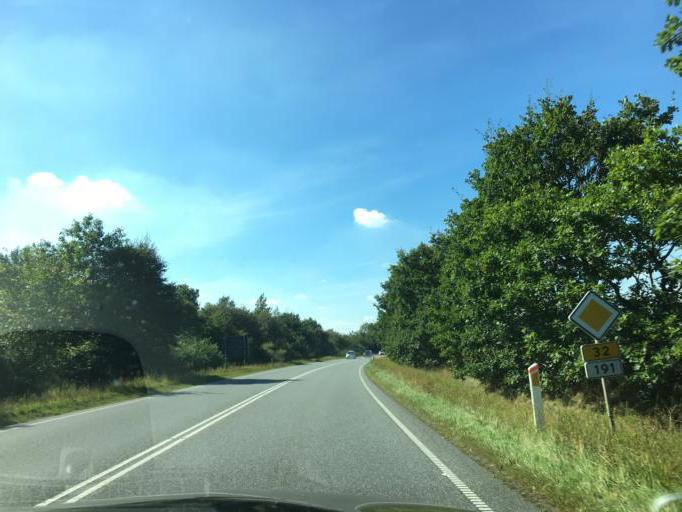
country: DK
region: South Denmark
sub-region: Kolding Kommune
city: Lunderskov
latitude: 55.4854
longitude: 9.2833
